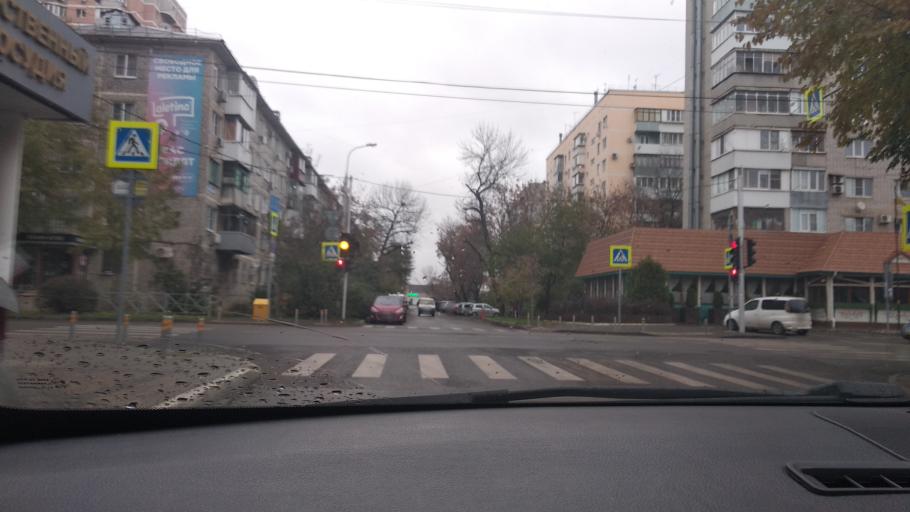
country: RU
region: Krasnodarskiy
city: Krasnodar
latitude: 45.0408
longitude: 38.9873
